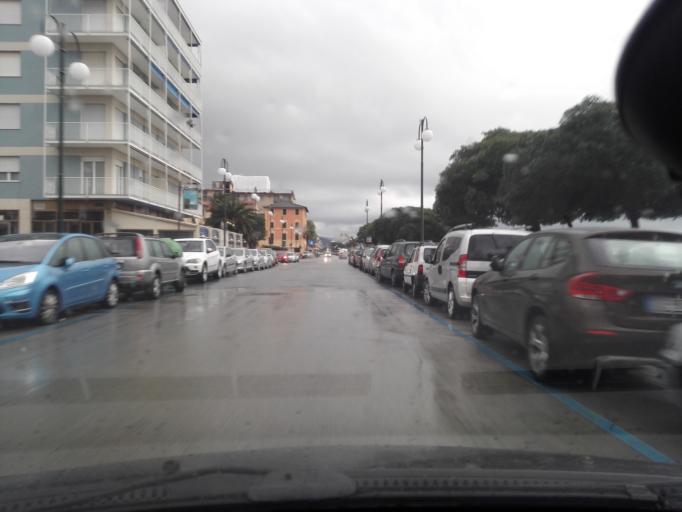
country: IT
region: Liguria
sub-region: Provincia di Genova
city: Chiavari
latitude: 44.3162
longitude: 9.3180
